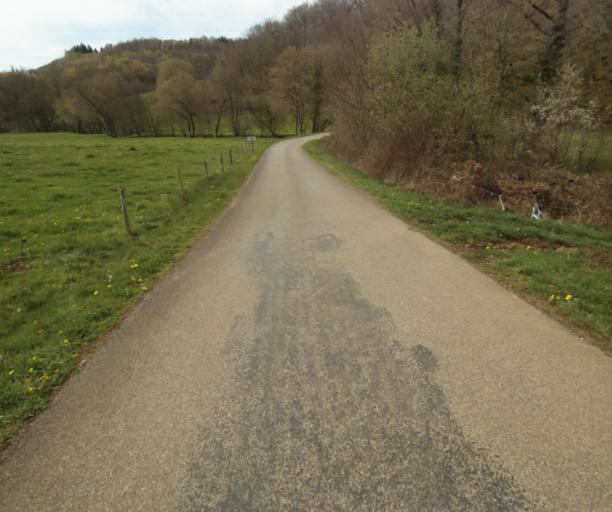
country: FR
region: Limousin
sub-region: Departement de la Correze
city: Laguenne
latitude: 45.2441
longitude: 1.8448
